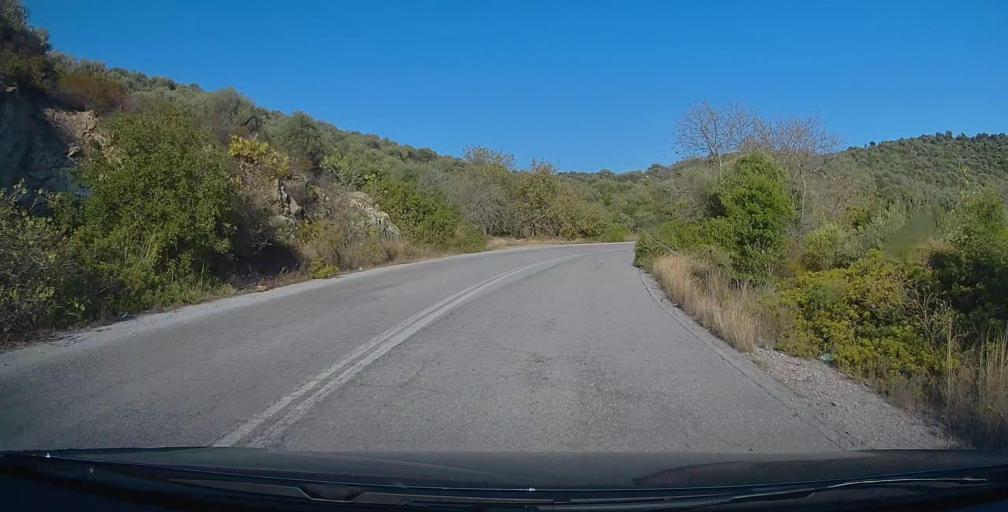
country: GR
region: Central Macedonia
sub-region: Nomos Chalkidikis
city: Sykia
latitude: 40.0142
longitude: 23.8730
